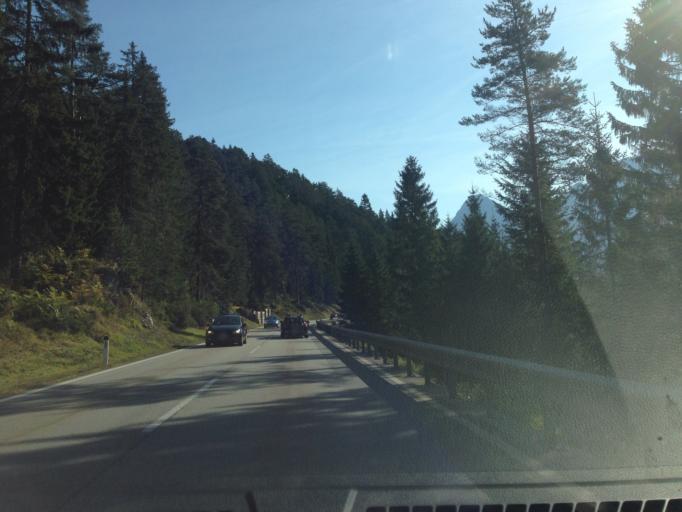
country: AT
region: Tyrol
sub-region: Politischer Bezirk Imst
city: Nassereith
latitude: 47.3637
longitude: 10.8342
